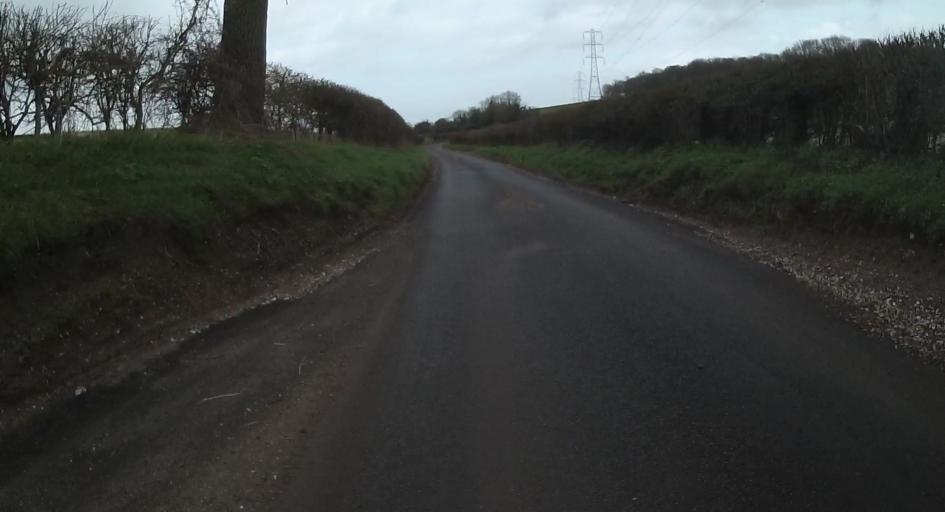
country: GB
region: England
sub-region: Hampshire
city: Kingsclere
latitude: 51.3047
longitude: -1.2186
